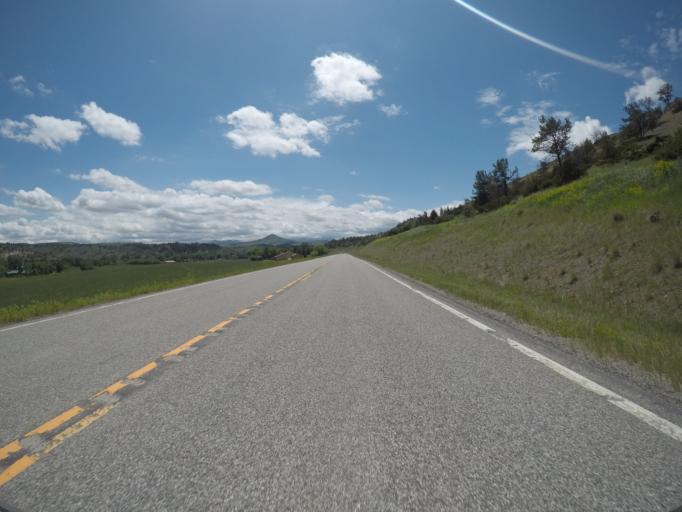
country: US
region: Montana
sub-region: Sweet Grass County
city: Big Timber
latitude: 45.7364
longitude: -109.9986
